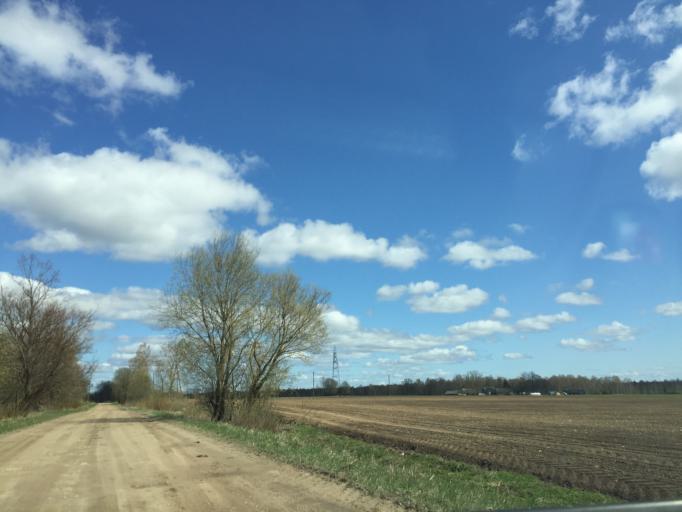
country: LV
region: Vilanu
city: Vilani
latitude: 56.6953
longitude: 27.1191
